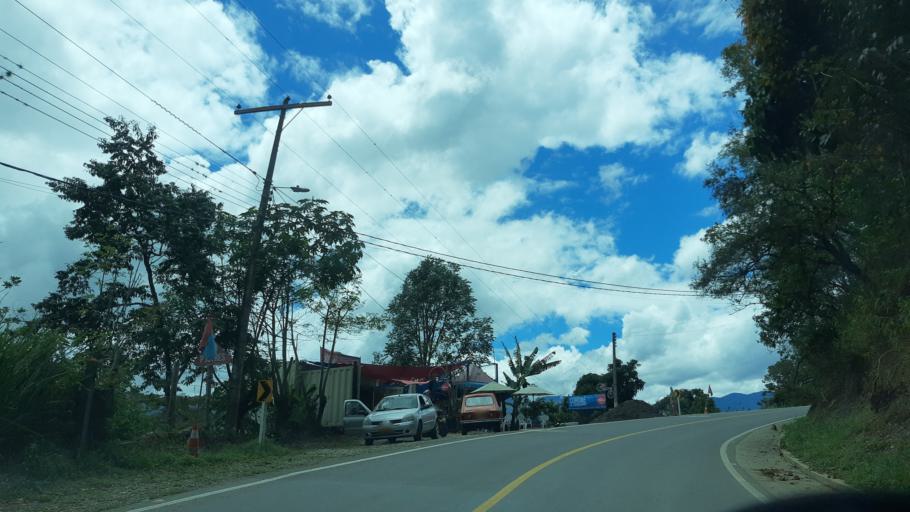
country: CO
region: Boyaca
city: Guateque
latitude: 5.0084
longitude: -73.4671
